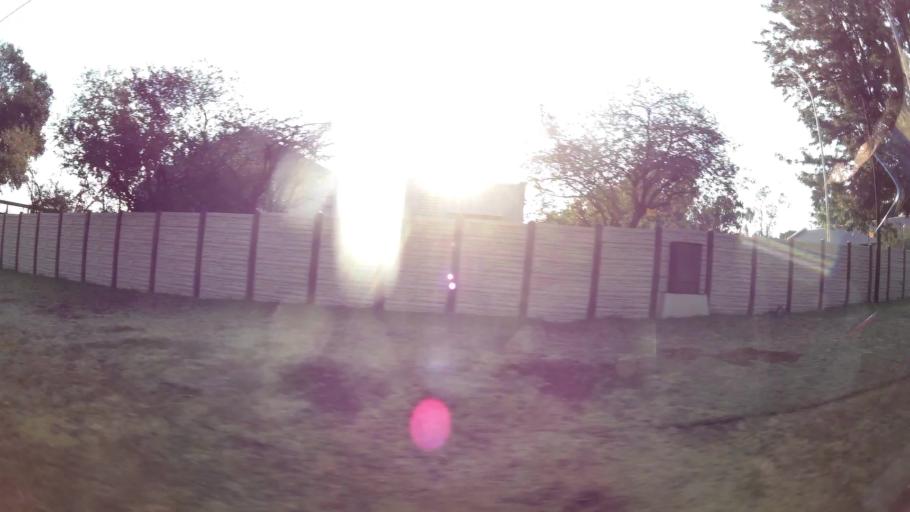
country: ZA
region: Gauteng
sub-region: Ekurhuleni Metropolitan Municipality
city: Benoni
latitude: -26.1556
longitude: 28.3661
